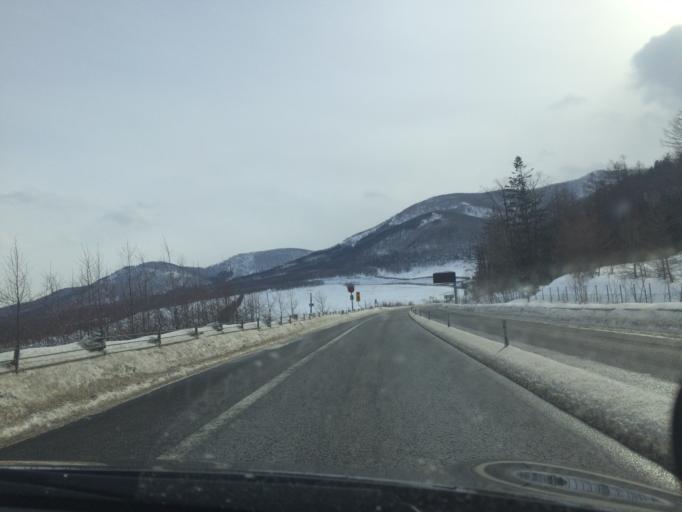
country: JP
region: Hokkaido
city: Otofuke
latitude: 43.0514
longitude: 142.7846
